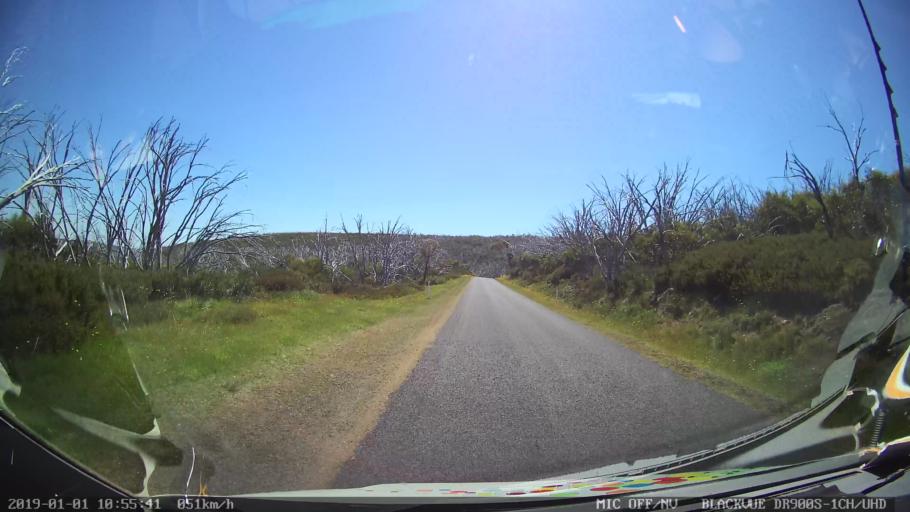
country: AU
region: New South Wales
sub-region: Snowy River
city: Jindabyne
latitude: -36.0082
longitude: 148.3907
